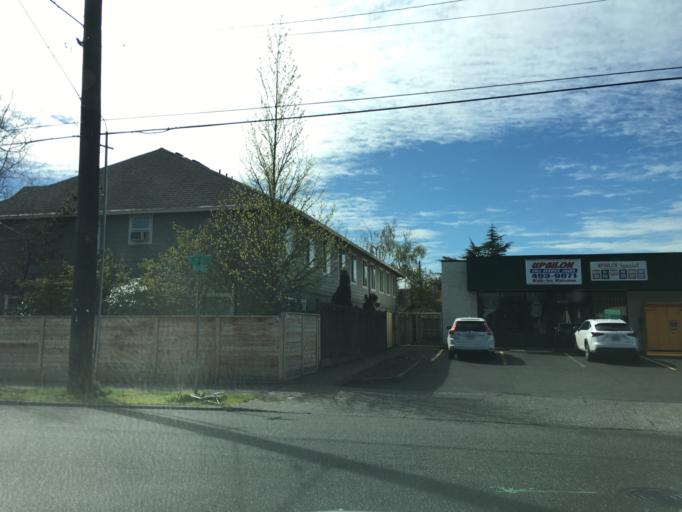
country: US
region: Oregon
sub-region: Multnomah County
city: Lents
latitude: 45.5337
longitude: -122.6016
